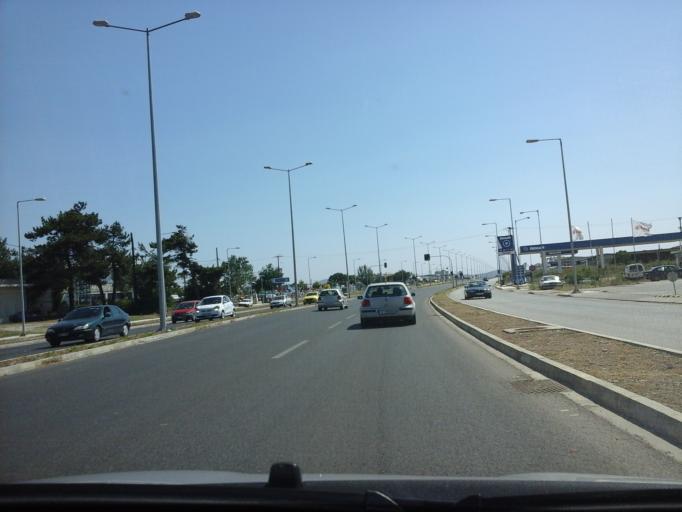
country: GR
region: East Macedonia and Thrace
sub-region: Nomos Evrou
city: Alexandroupoli
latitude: 40.8516
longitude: 25.9055
